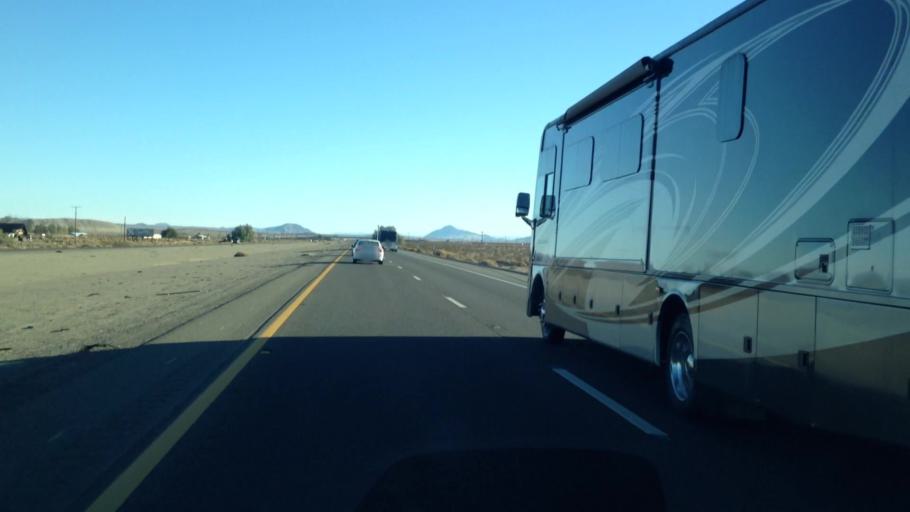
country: US
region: California
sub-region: San Bernardino County
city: Fort Irwin
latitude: 34.9560
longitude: -116.6620
